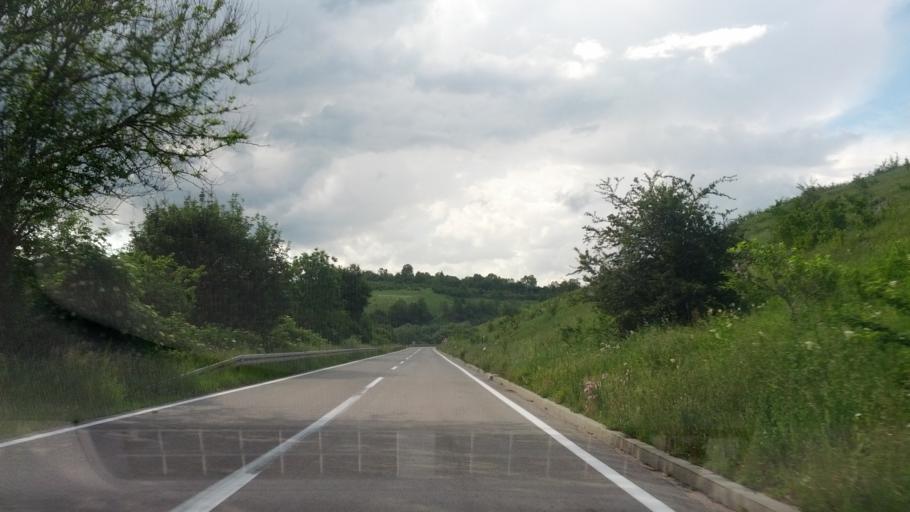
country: BA
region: Federation of Bosnia and Herzegovina
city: Izacic
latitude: 44.9158
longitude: 15.7168
